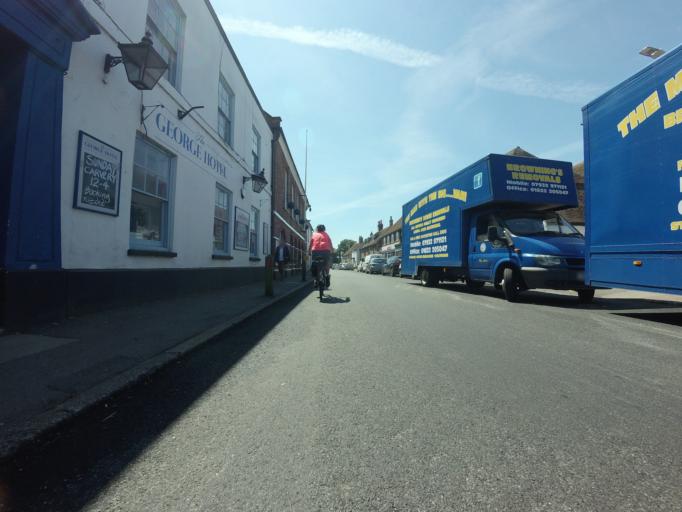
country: GB
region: England
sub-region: Kent
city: Lydd
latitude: 50.9514
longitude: 0.9056
